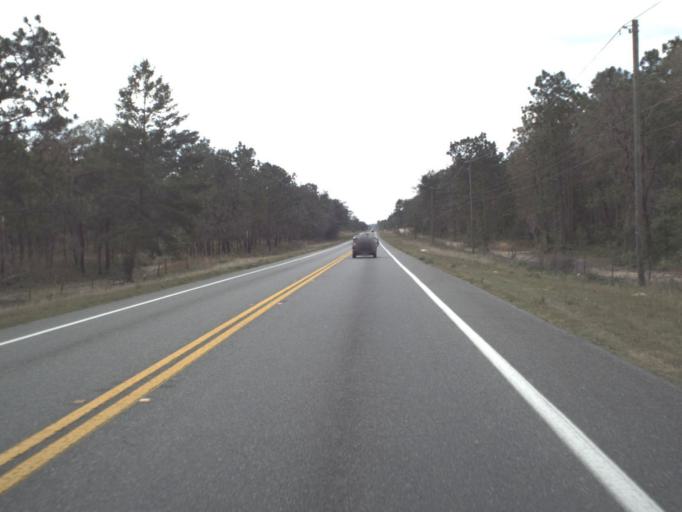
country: US
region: Florida
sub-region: Marion County
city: Ocala
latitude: 29.2528
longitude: -82.0669
